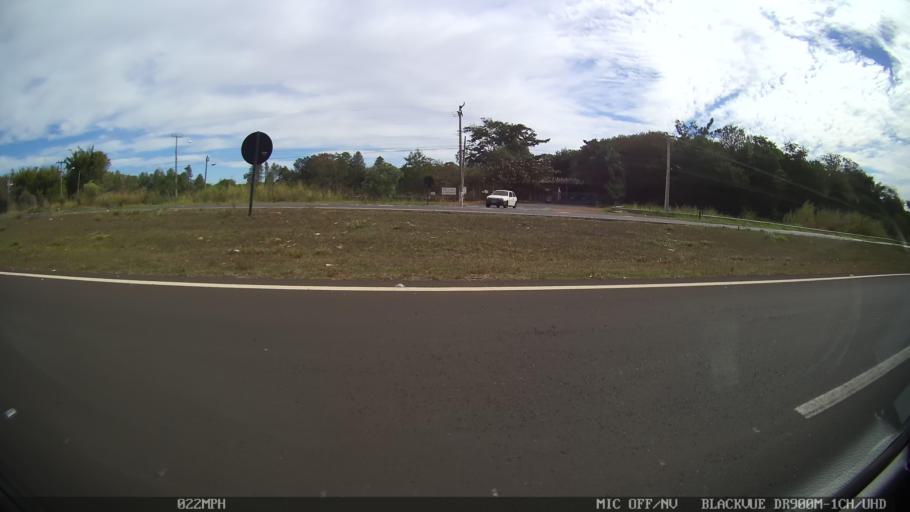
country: BR
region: Sao Paulo
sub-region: Catanduva
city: Catanduva
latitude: -21.1645
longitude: -48.9879
